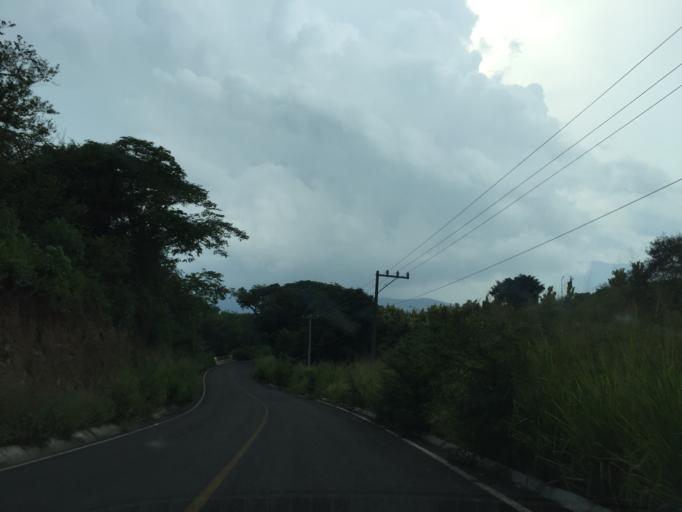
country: MX
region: Colima
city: Comala
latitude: 19.3362
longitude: -103.7722
